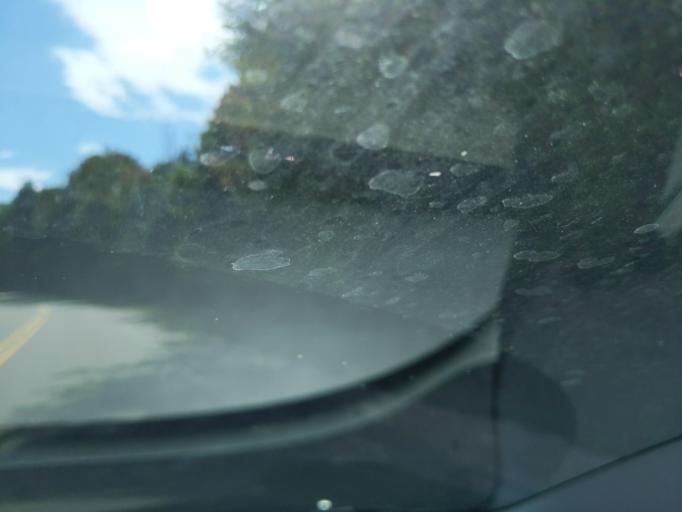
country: US
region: Michigan
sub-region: Antrim County
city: Bellaire
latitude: 45.0581
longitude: -85.3190
